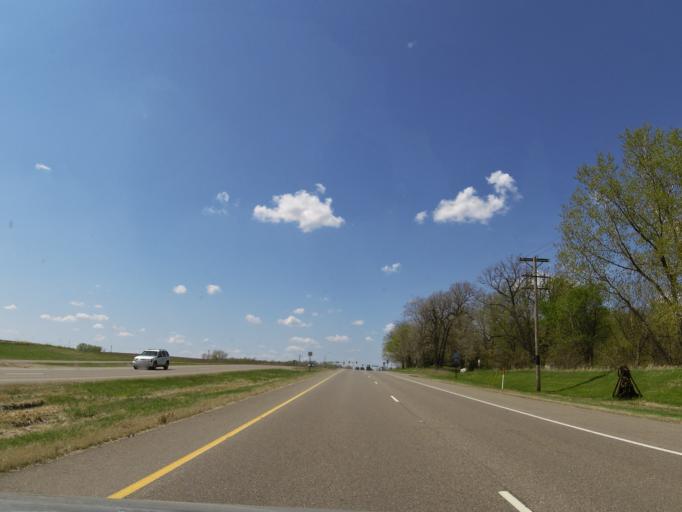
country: US
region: Minnesota
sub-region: Scott County
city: Prior Lake
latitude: 44.7468
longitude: -93.4351
